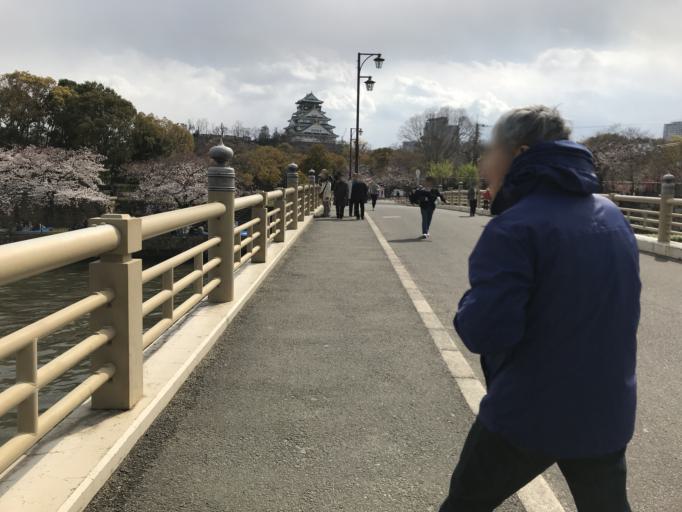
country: JP
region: Osaka
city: Osaka-shi
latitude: 34.6912
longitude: 135.5278
